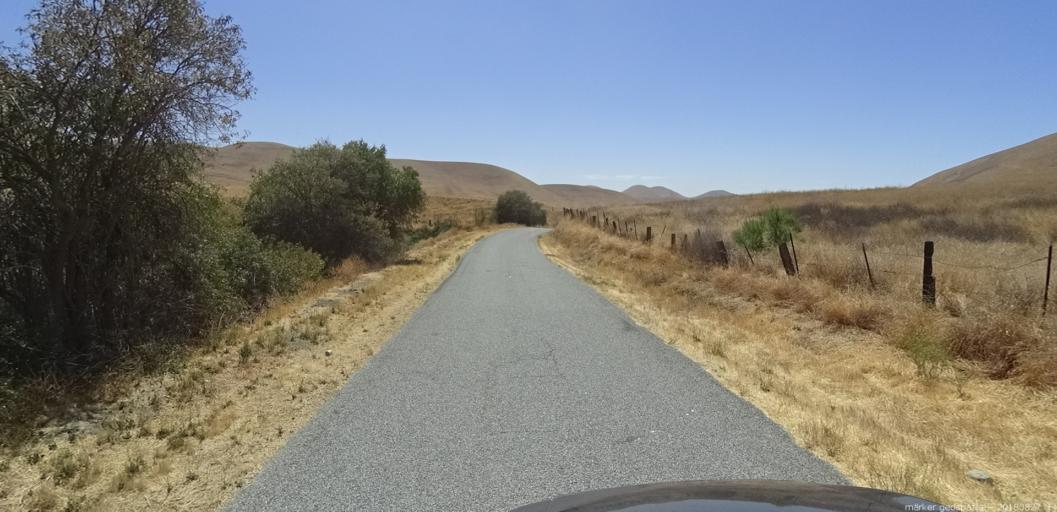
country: US
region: California
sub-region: Monterey County
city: King City
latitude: 36.1175
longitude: -120.8733
